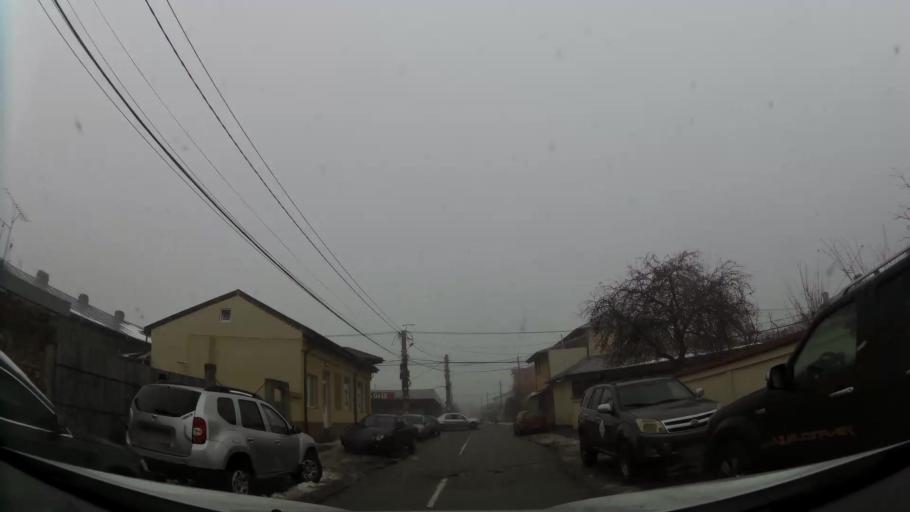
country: RO
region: Ilfov
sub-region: Comuna Chiajna
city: Chiajna
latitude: 44.4594
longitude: 25.9732
